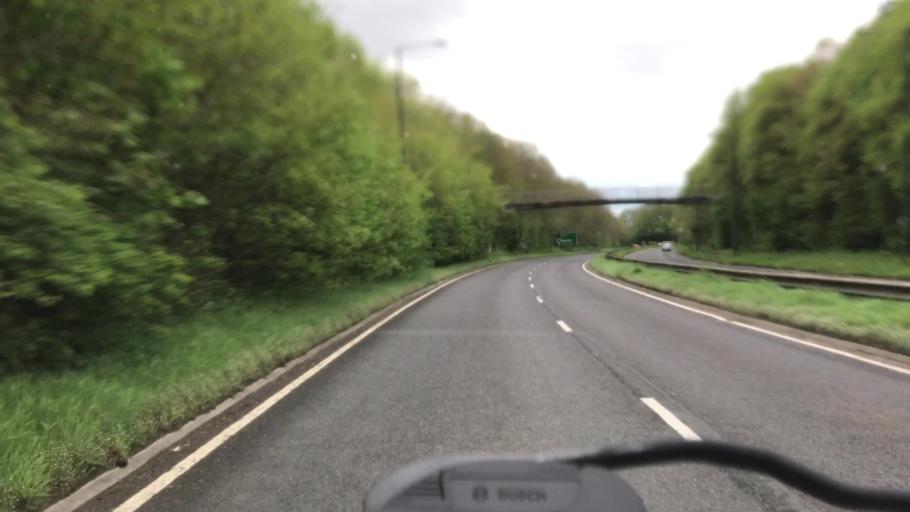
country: GB
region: England
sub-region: Gloucestershire
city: Cirencester
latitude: 51.7122
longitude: -1.9543
